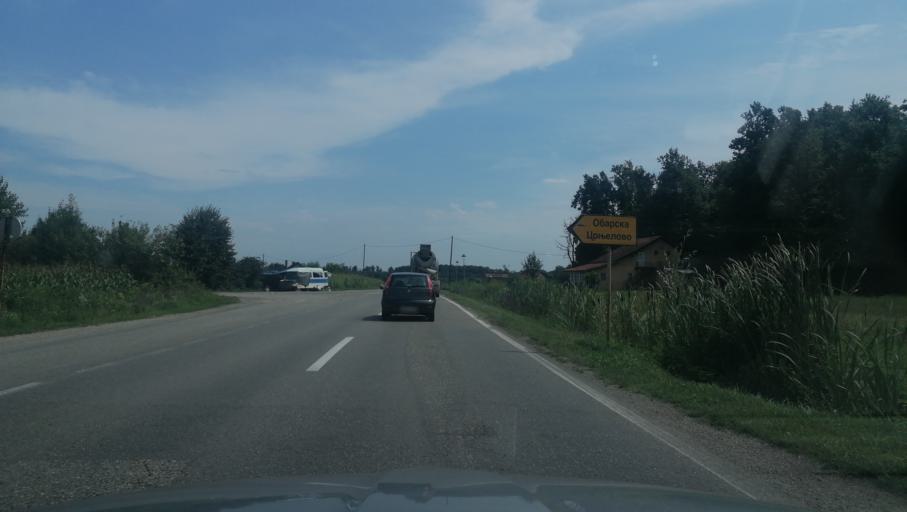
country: BA
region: Republika Srpska
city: Velika Obarska
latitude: 44.7733
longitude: 19.1181
